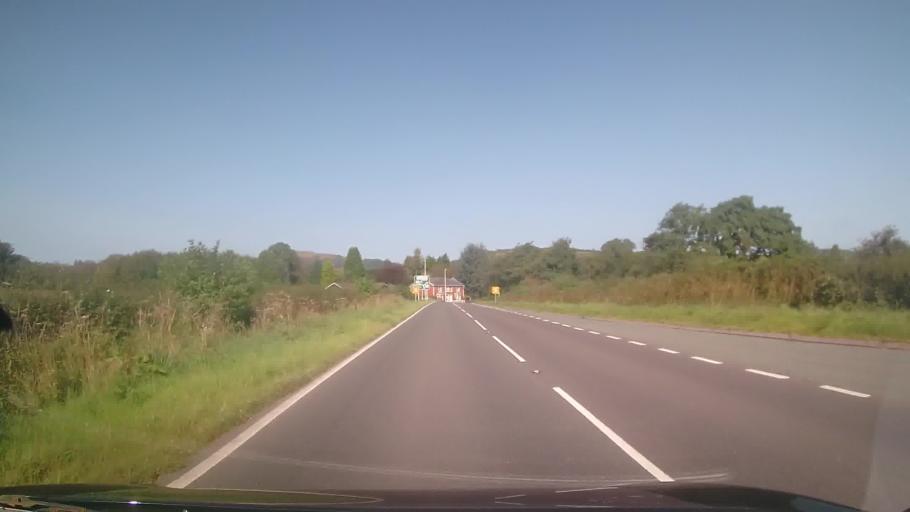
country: GB
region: Wales
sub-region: Sir Powys
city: Rhayader
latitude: 52.1464
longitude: -3.5773
